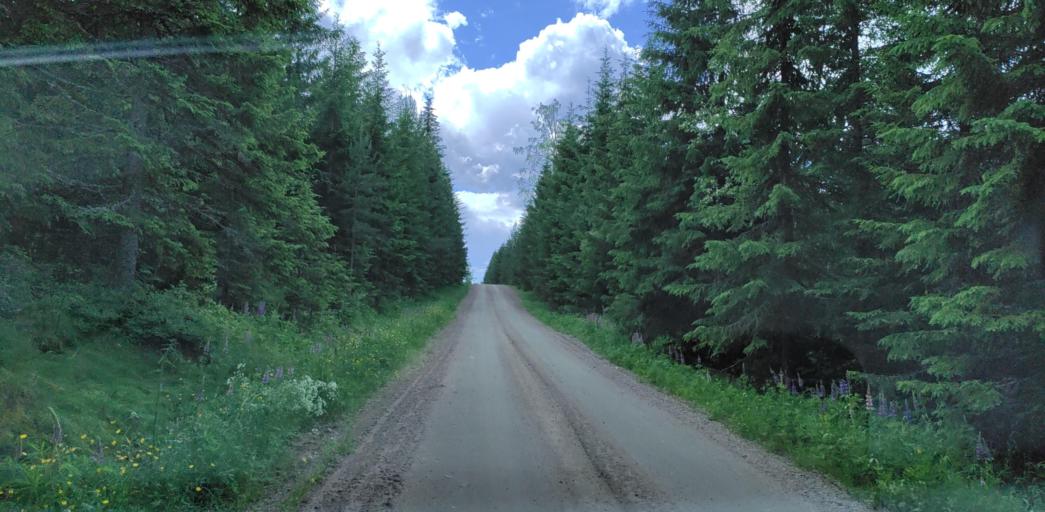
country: SE
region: Vaermland
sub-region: Hagfors Kommun
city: Ekshaerad
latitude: 60.0948
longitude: 13.3457
